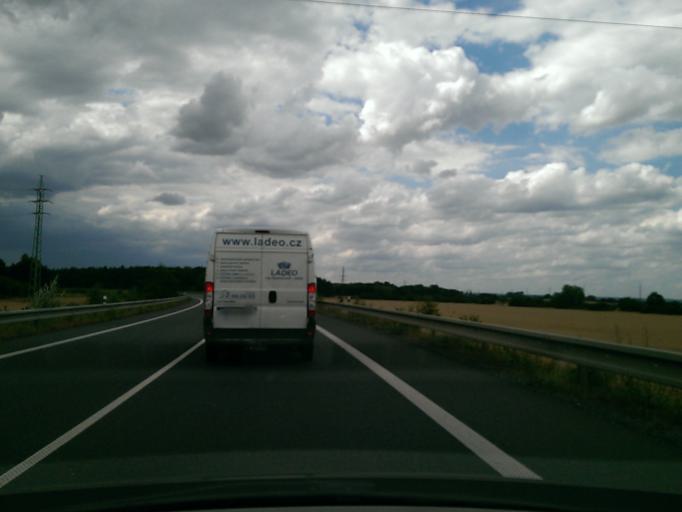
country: CZ
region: Central Bohemia
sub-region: Okres Nymburk
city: Podebrady
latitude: 50.1761
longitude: 15.0908
